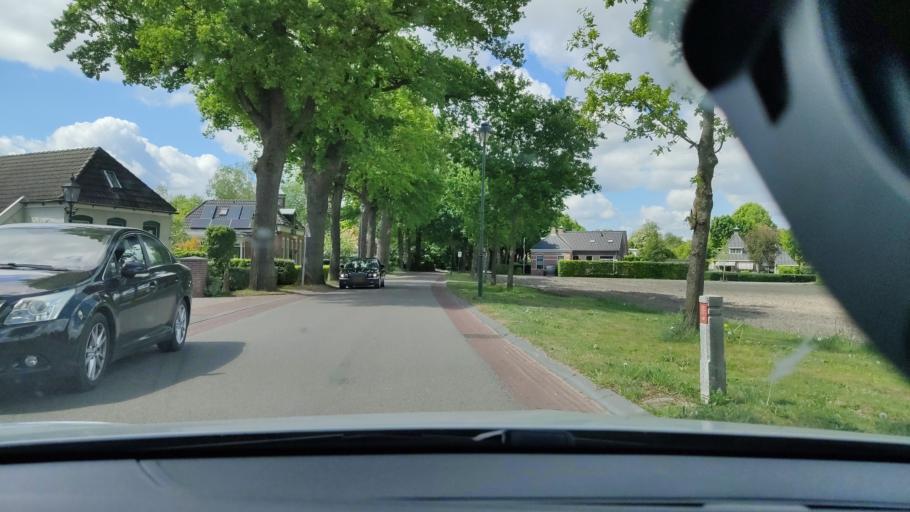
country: NL
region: Drenthe
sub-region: Gemeente Tynaarlo
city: Zuidlaren
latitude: 53.1172
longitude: 6.6687
